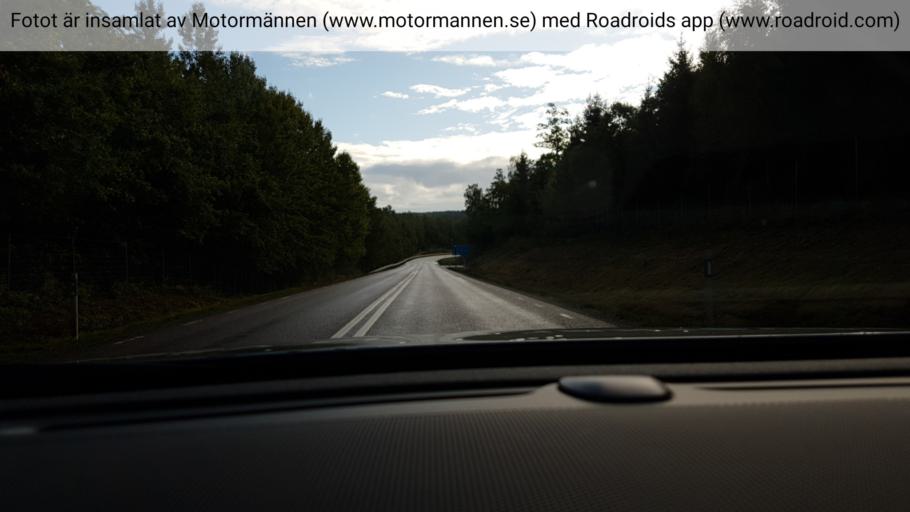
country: SE
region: Vaestra Goetaland
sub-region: Harryda Kommun
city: Ravlanda
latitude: 57.6213
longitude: 12.4253
